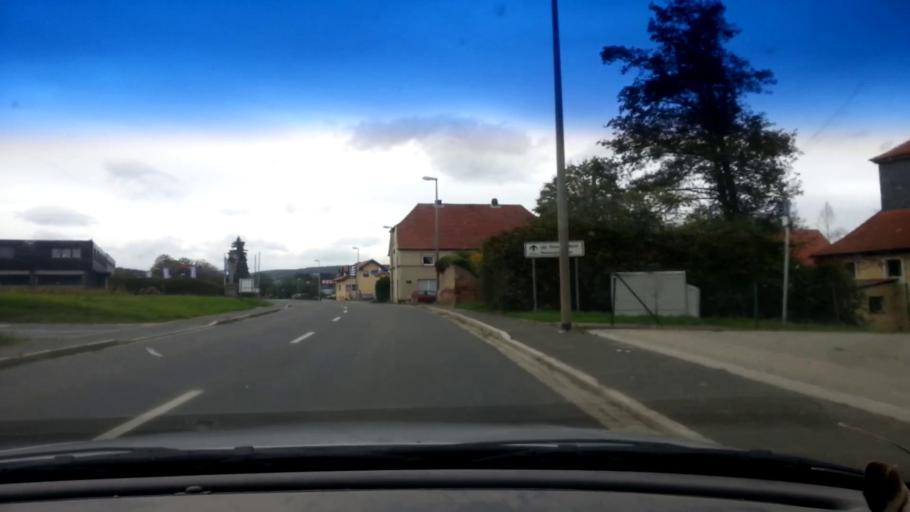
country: DE
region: Bavaria
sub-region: Upper Franconia
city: Baunach
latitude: 49.9895
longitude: 10.8465
